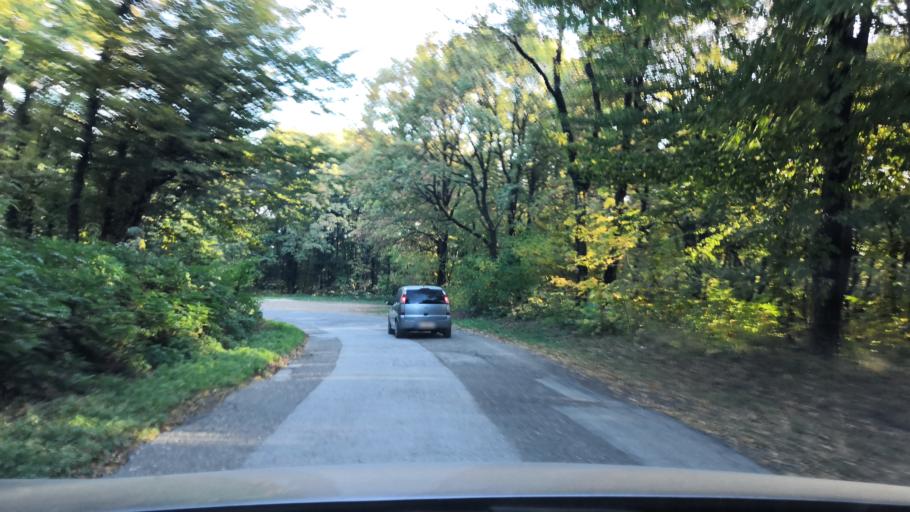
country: RS
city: Vrdnik
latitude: 45.1502
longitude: 19.8237
